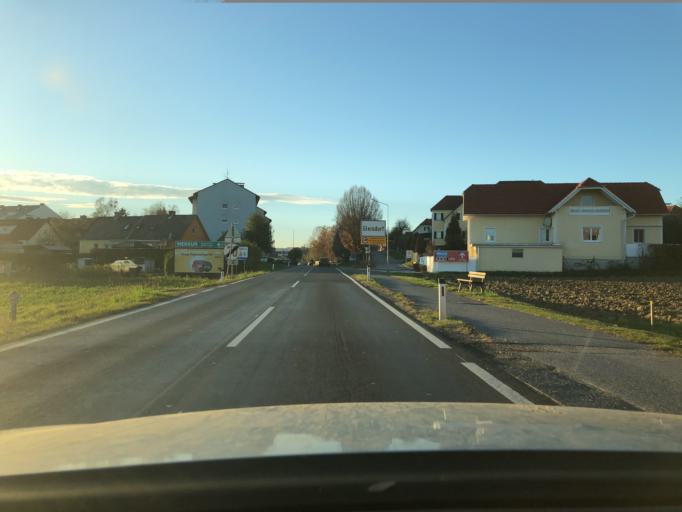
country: AT
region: Styria
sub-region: Politischer Bezirk Weiz
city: Gleisdorf
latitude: 47.1018
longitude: 15.7229
